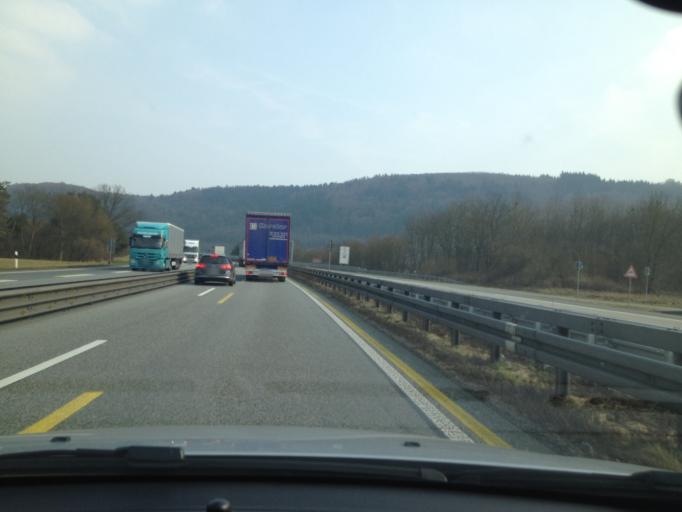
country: DE
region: Hesse
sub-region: Regierungsbezirk Giessen
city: Haiger
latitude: 50.7449
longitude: 8.2348
